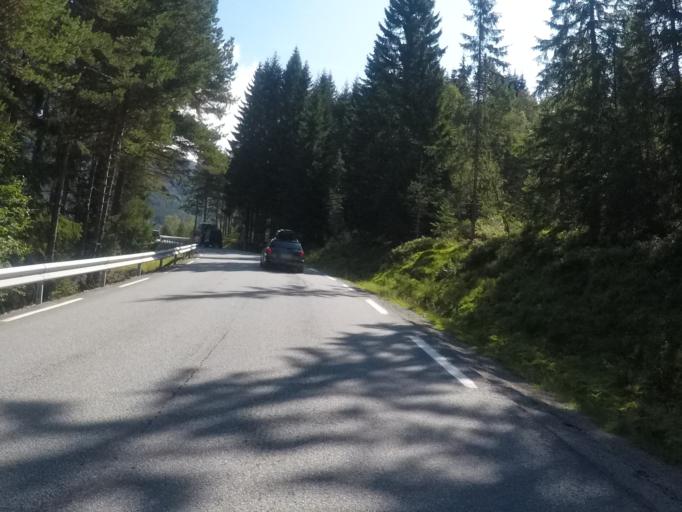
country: NO
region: Sogn og Fjordane
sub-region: Hornindal
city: Hornindal
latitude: 61.7947
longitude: 6.5303
